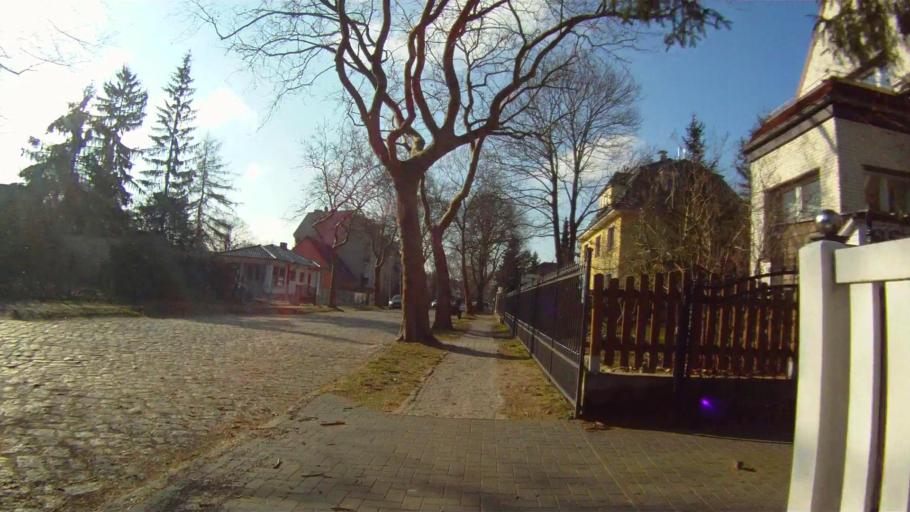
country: DE
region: Berlin
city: Rahnsdorf
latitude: 52.4442
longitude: 13.6908
